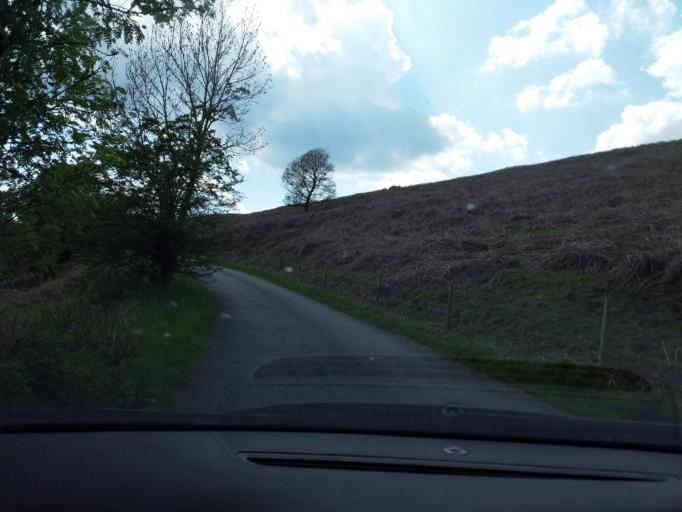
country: GB
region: England
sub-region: Derbyshire
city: Hathersage
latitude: 53.3534
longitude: -1.6733
